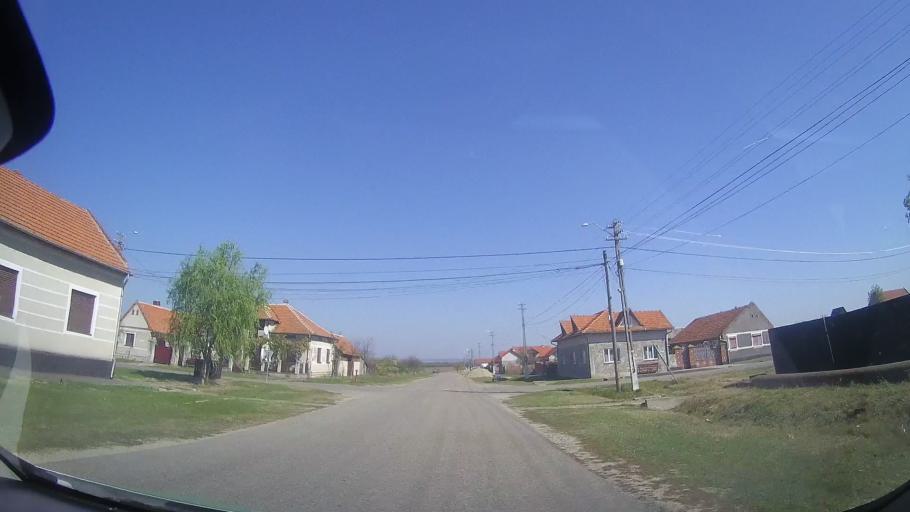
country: RO
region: Timis
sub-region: Comuna Bethausen
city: Bethausen
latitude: 45.8004
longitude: 21.9975
